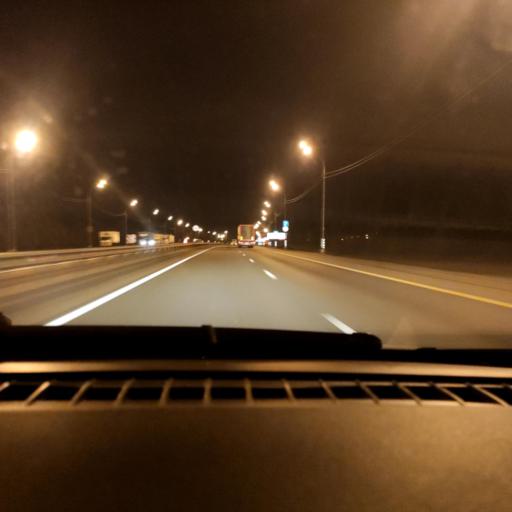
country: RU
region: Lipetsk
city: Khlevnoye
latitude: 52.1322
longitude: 39.1985
